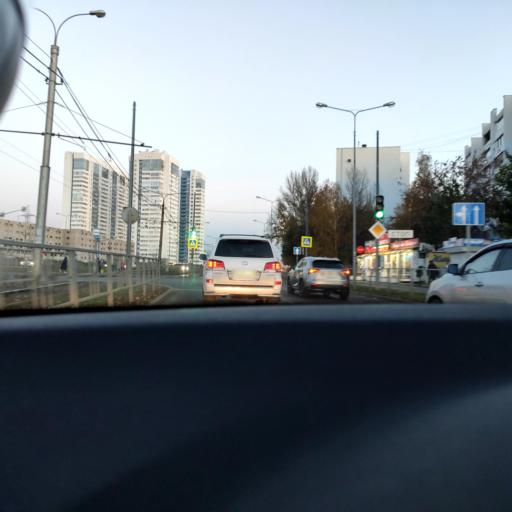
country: RU
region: Samara
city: Samara
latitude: 53.2675
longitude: 50.2266
